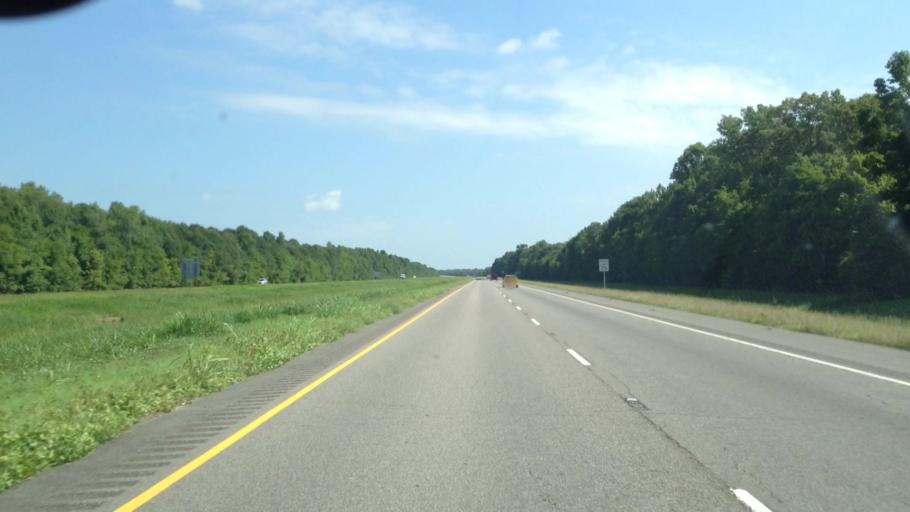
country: US
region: Louisiana
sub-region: Avoyelles Parish
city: Bunkie
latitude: 30.8768
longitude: -92.2273
